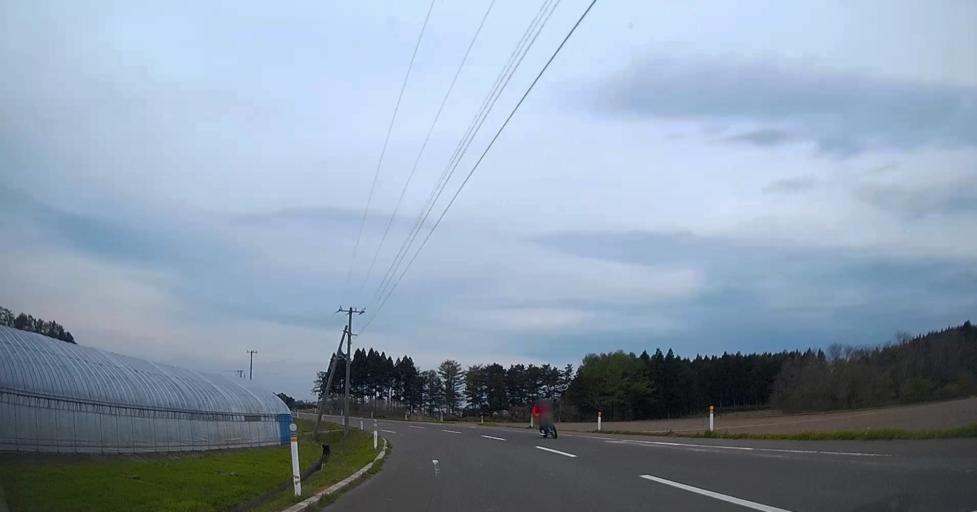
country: JP
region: Aomori
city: Goshogawara
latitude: 40.9023
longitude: 140.4942
